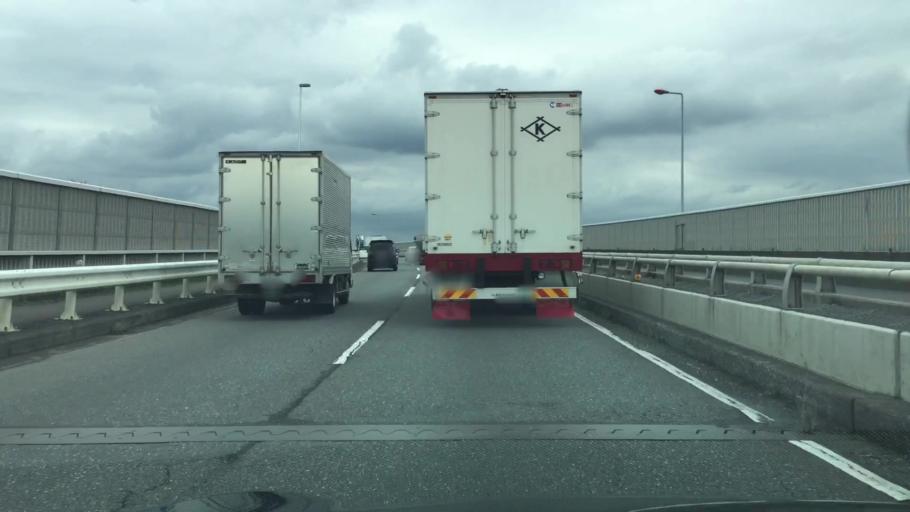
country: JP
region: Saitama
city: Kamifukuoka
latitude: 35.9127
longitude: 139.5358
